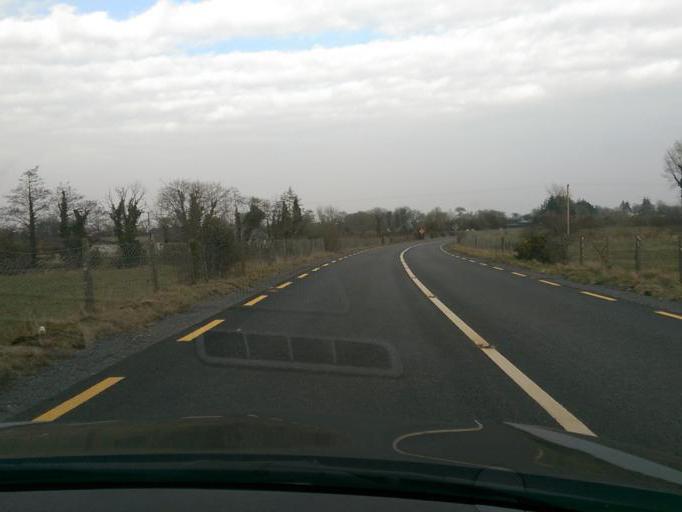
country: IE
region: Connaught
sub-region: Roscommon
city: Castlerea
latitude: 53.5043
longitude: -8.4603
